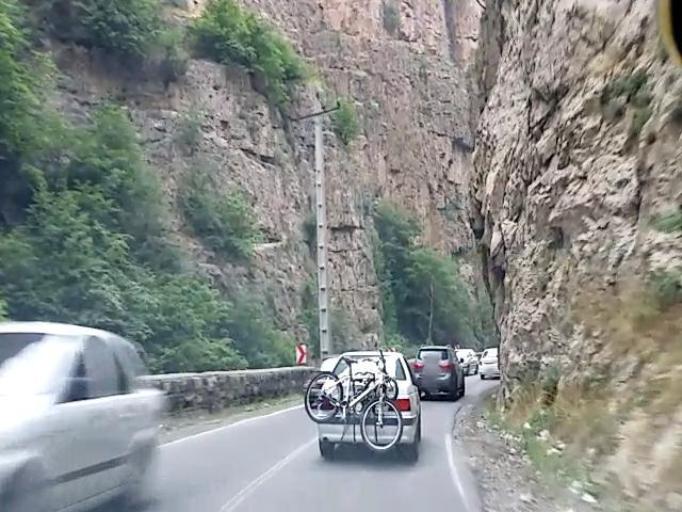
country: IR
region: Mazandaran
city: Chalus
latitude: 36.2736
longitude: 51.2440
